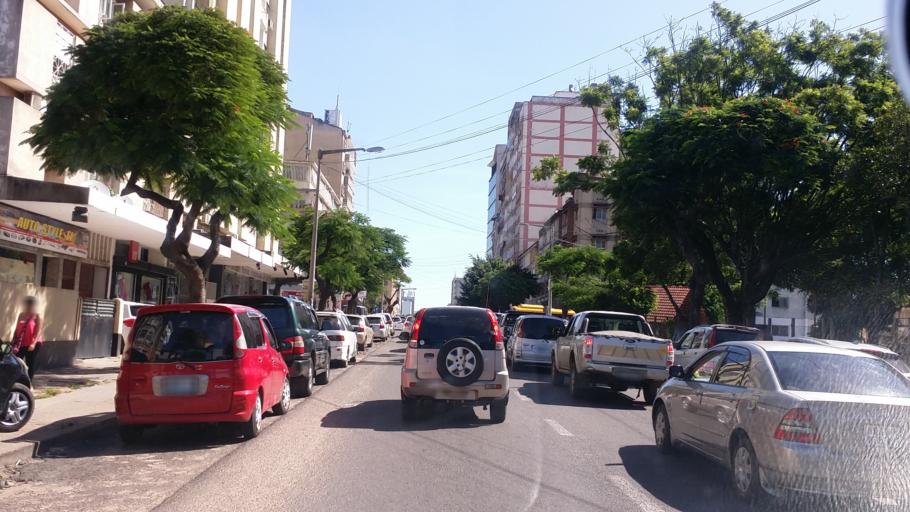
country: MZ
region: Maputo City
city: Maputo
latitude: -25.9640
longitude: 32.5808
